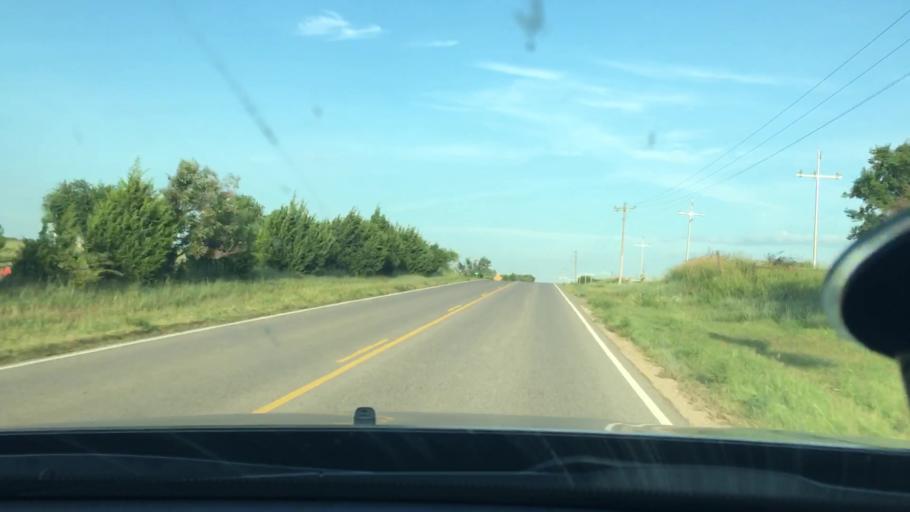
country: US
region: Oklahoma
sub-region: Garvin County
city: Stratford
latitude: 34.7967
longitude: -96.8953
